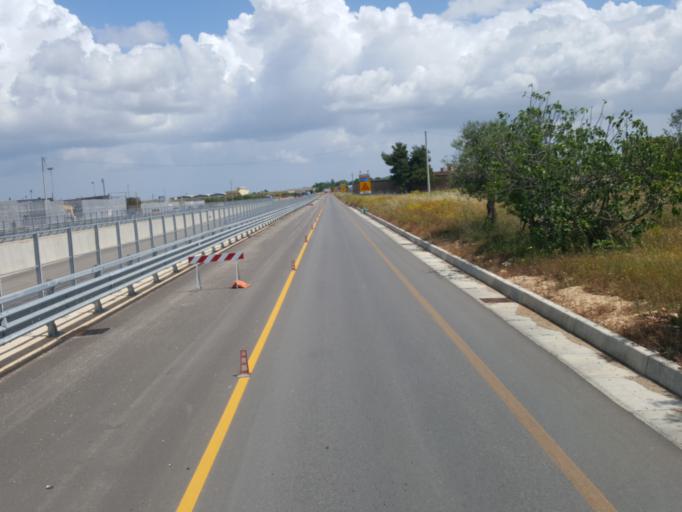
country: IT
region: Apulia
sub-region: Provincia di Bari
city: Bitetto
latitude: 41.0713
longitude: 16.7432
